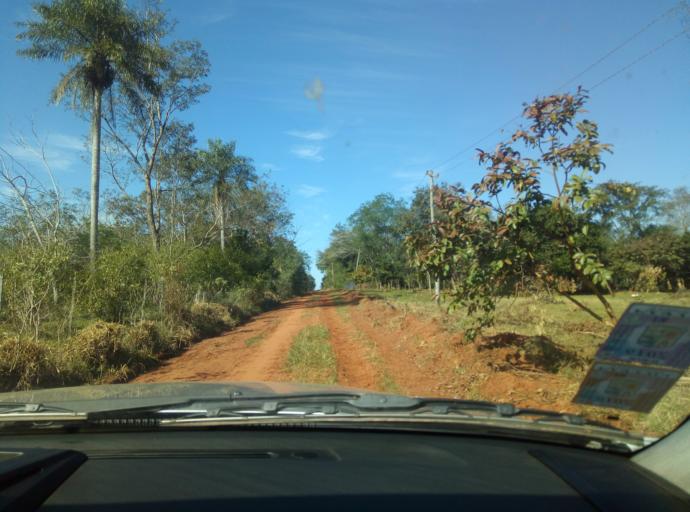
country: PY
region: Caaguazu
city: Carayao
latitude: -25.1703
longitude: -56.2987
